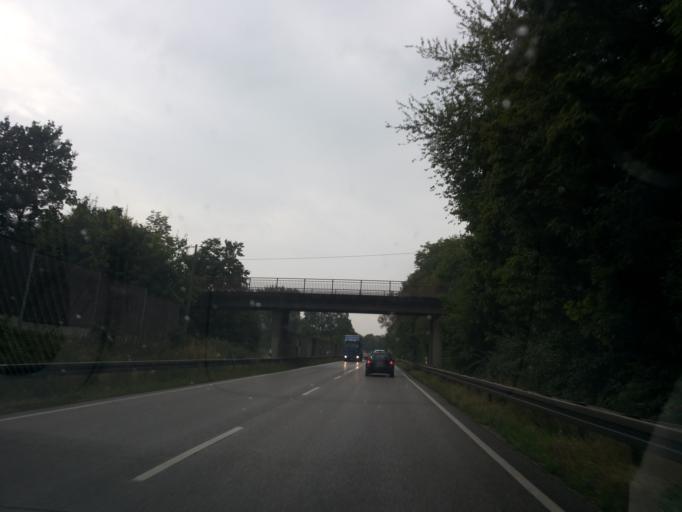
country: DE
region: Bavaria
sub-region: Upper Bavaria
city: Lenting
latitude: 48.7760
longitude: 11.4873
